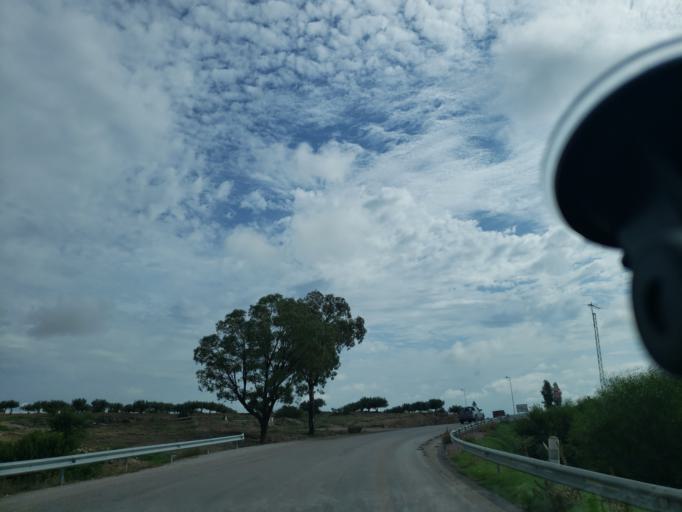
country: TN
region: Zaghwan
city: El Fahs
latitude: 36.3945
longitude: 9.9080
